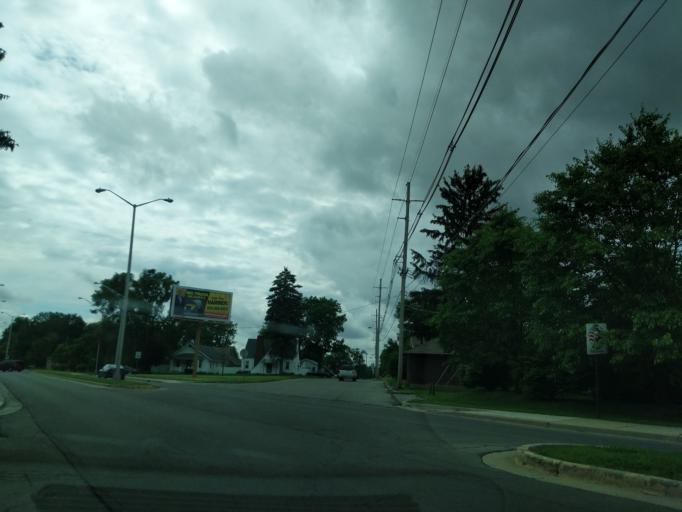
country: US
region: Indiana
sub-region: Madison County
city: Anderson
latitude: 40.0974
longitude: -85.6863
